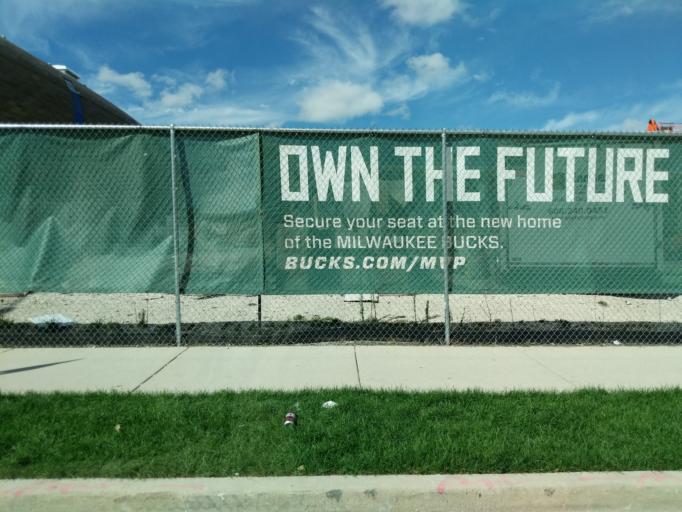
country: US
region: Wisconsin
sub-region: Milwaukee County
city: Milwaukee
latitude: 43.0460
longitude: -87.9161
